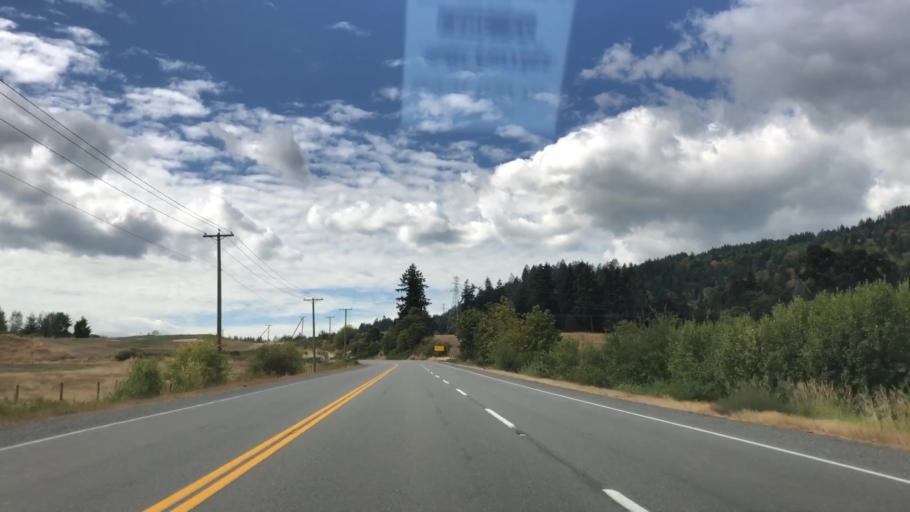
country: CA
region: British Columbia
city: Duncan
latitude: 48.8141
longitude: -123.7409
